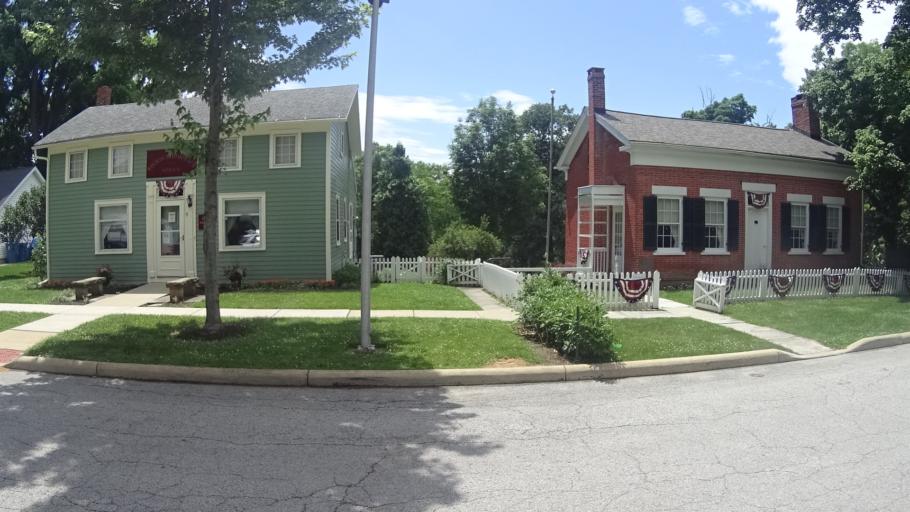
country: US
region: Ohio
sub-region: Erie County
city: Milan
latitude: 41.3000
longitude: -82.6043
